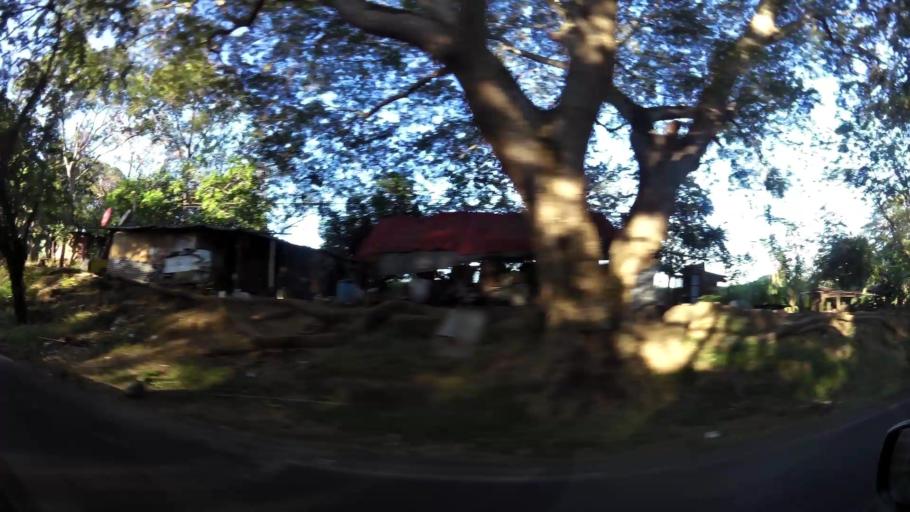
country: CR
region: Puntarenas
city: Esparza
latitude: 10.0008
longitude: -84.7201
